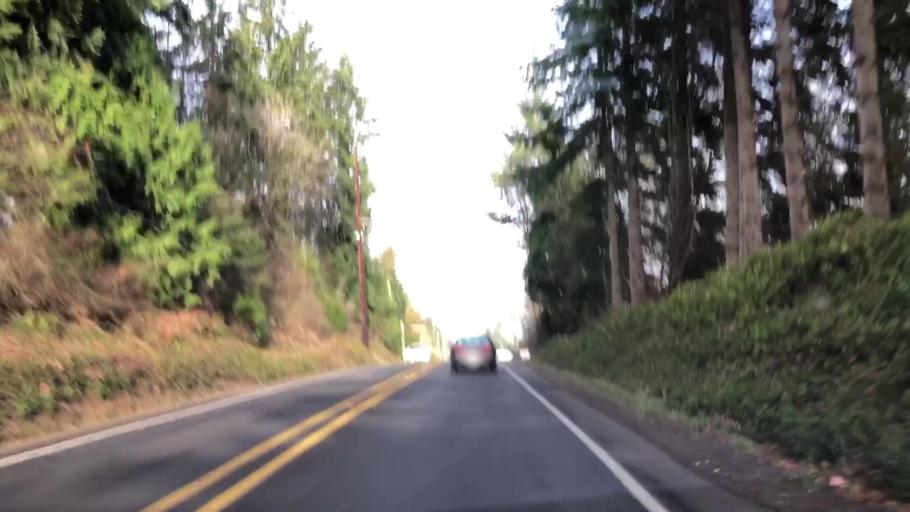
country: US
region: Washington
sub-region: Kitsap County
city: Kingston
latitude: 47.7924
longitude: -122.5415
